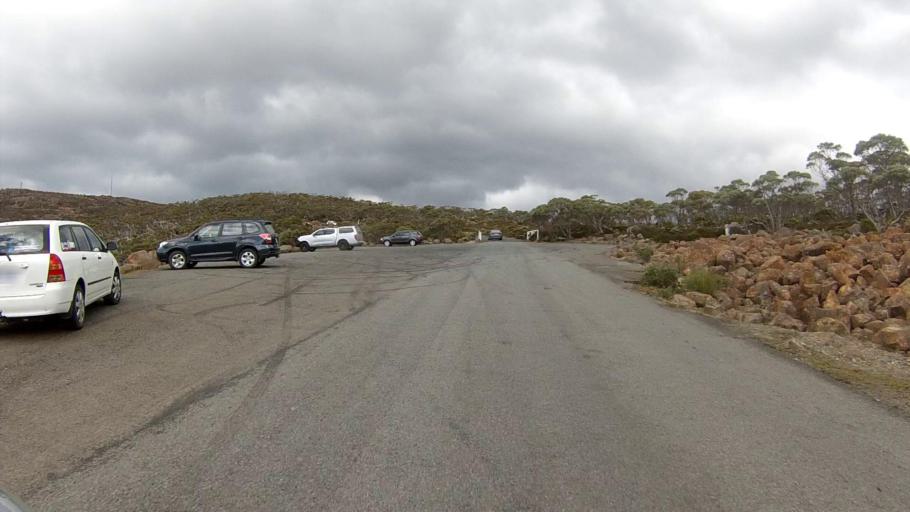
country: AU
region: Tasmania
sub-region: Glenorchy
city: West Moonah
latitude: -42.8891
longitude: 147.2208
